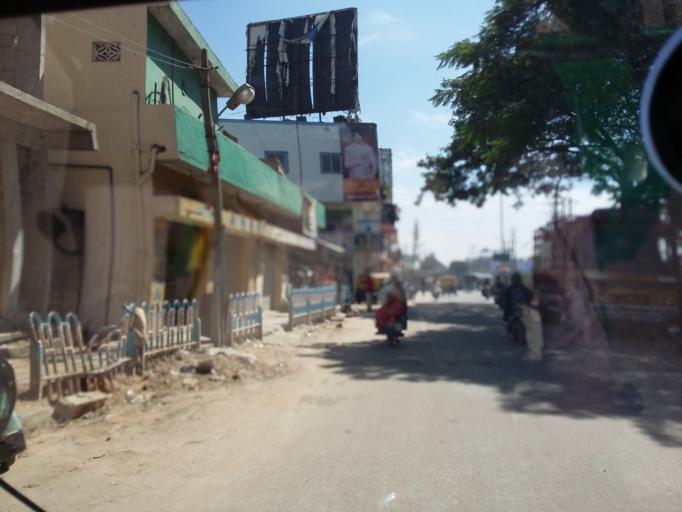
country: IN
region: Karnataka
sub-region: Bangalore Urban
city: Bangalore
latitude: 12.9529
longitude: 77.6193
